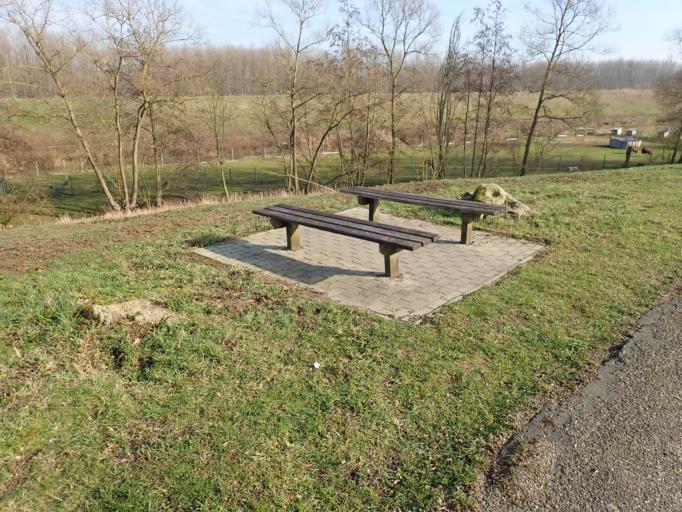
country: BE
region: Flanders
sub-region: Provincie Oost-Vlaanderen
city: Dendermonde
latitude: 51.0532
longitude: 4.1344
